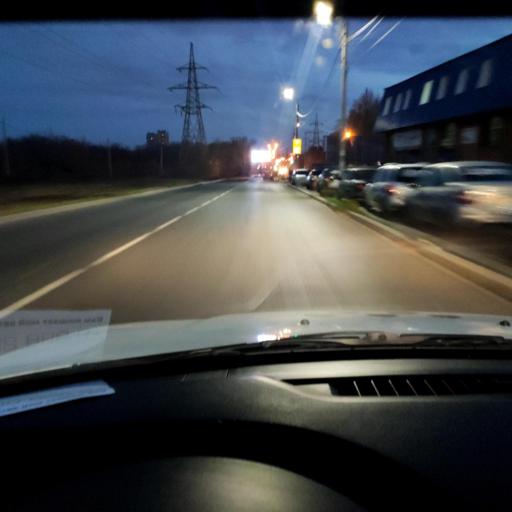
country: RU
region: Samara
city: Tol'yatti
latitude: 53.5234
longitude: 49.3959
